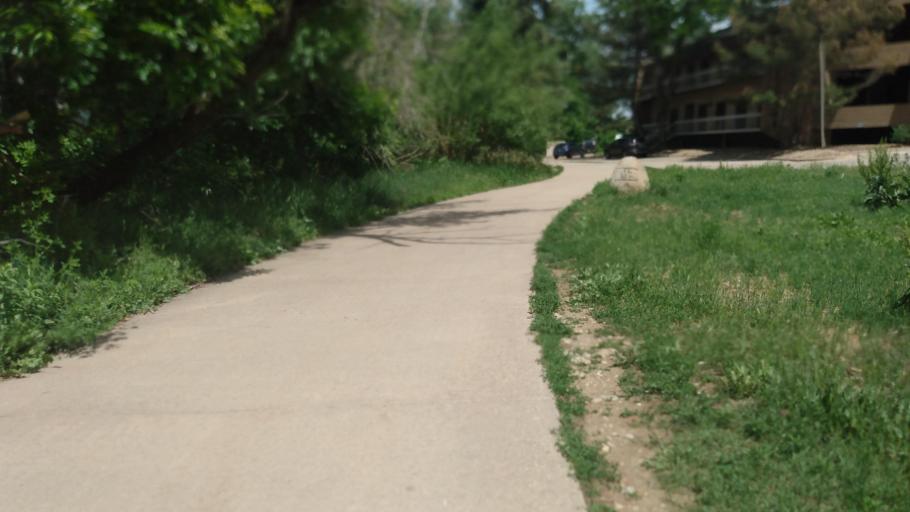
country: US
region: Colorado
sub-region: Boulder County
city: Boulder
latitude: 40.0151
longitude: -105.2436
